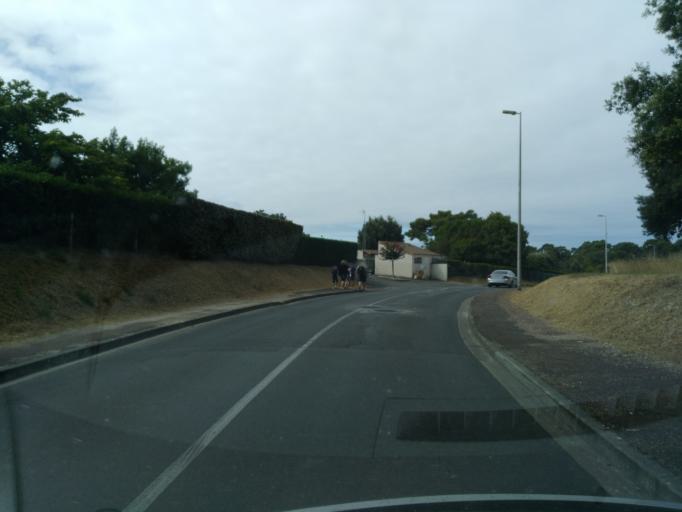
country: FR
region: Poitou-Charentes
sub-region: Departement de la Charente-Maritime
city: Saint-Palais-sur-Mer
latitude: 45.6472
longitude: -1.0879
